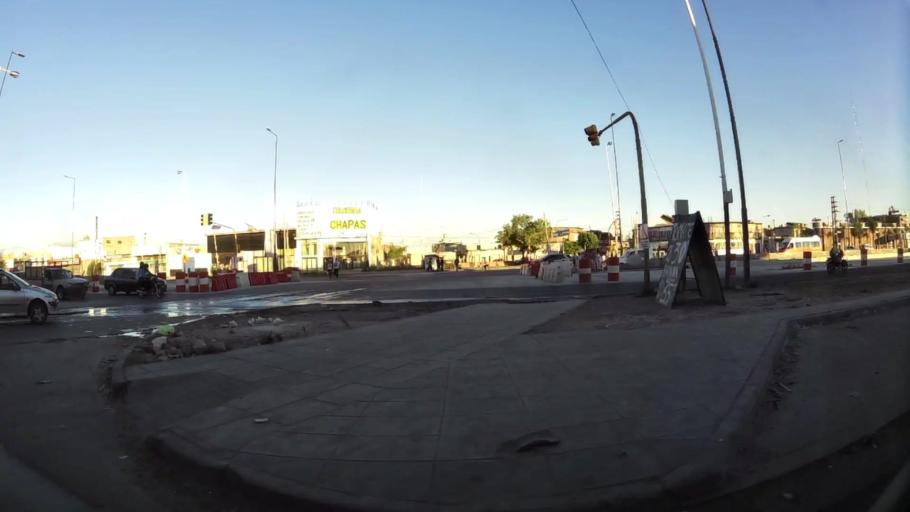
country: AR
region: Buenos Aires
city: San Justo
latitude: -34.7359
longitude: -58.6039
